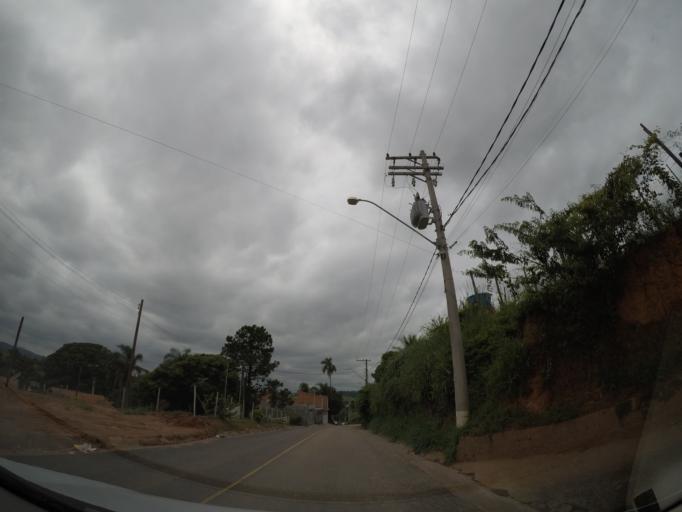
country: BR
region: Sao Paulo
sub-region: Louveira
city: Louveira
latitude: -23.0985
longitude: -46.9965
